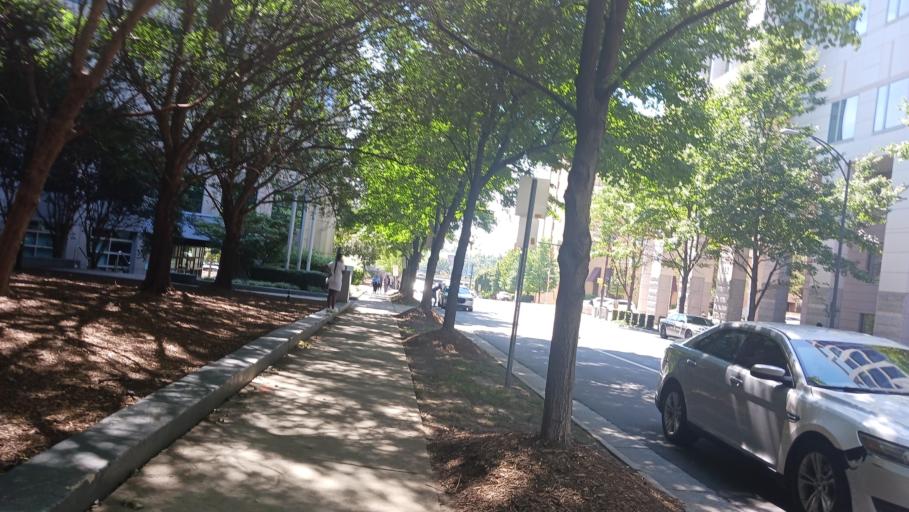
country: US
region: North Carolina
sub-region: Mecklenburg County
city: Charlotte
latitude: 35.2203
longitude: -80.8369
